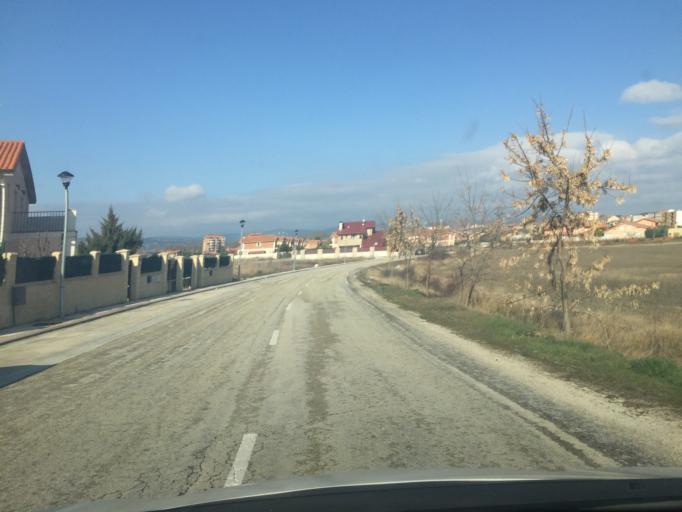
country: ES
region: Castille and Leon
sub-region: Provincia de Burgos
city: Medina de Pomar
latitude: 42.9307
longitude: -3.5790
